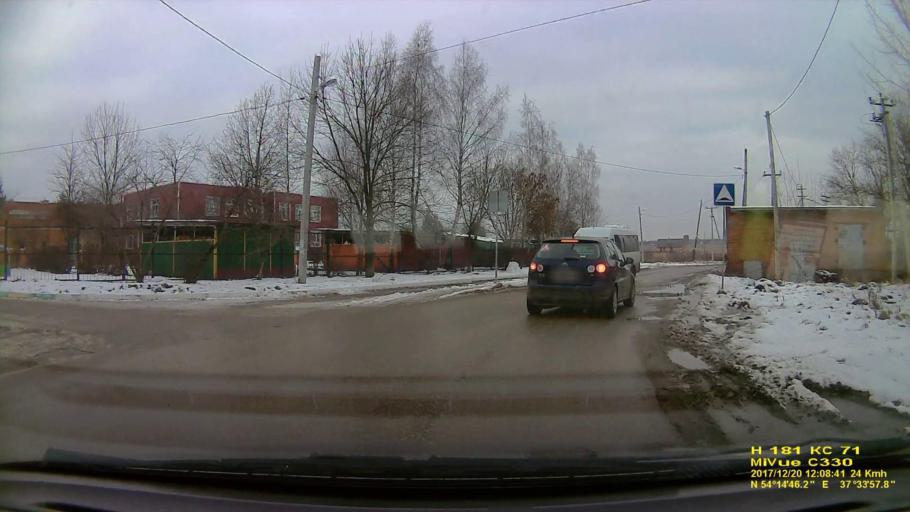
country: RU
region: Tula
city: Gorelki
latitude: 54.2462
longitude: 37.5661
